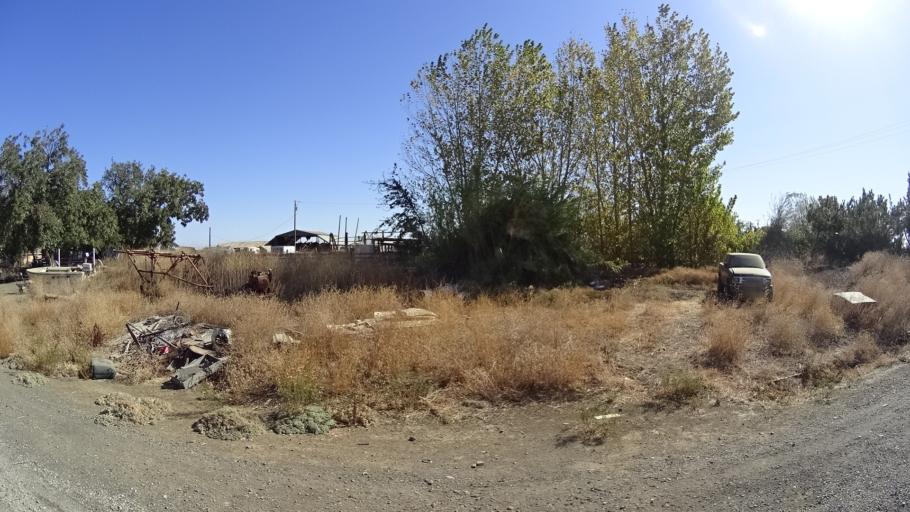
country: US
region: California
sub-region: Yolo County
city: Winters
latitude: 38.5510
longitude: -121.9712
